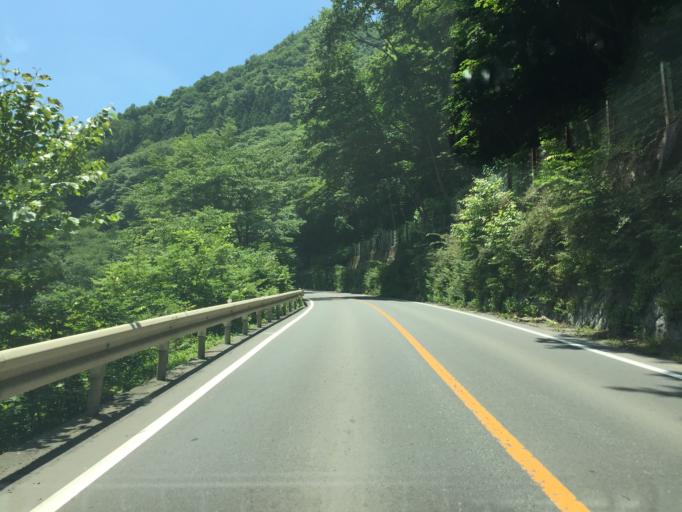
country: JP
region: Miyagi
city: Marumori
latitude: 37.7730
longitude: 140.7979
